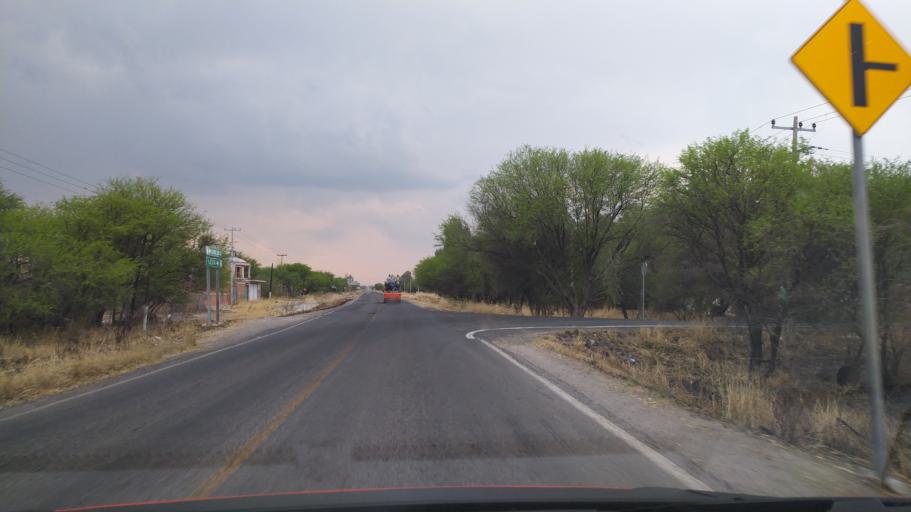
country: MX
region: Guanajuato
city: Ciudad Manuel Doblado
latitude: 20.7924
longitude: -101.9064
